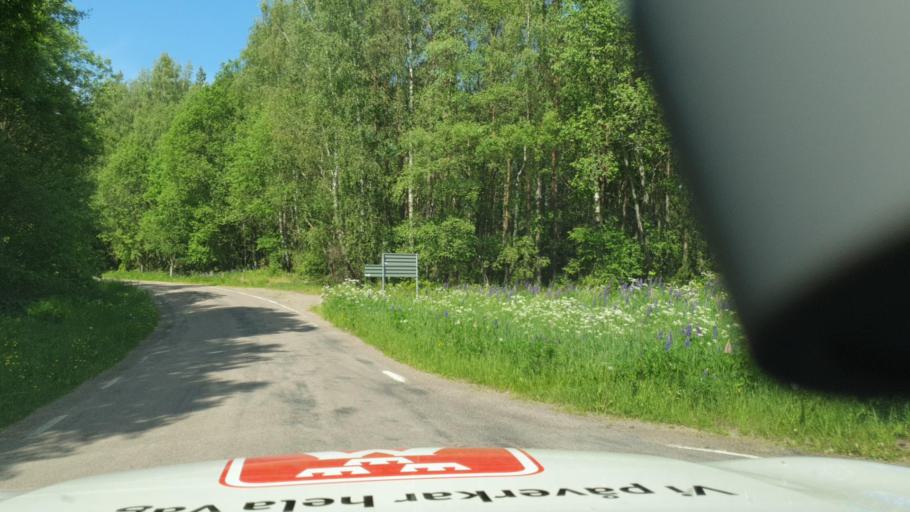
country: SE
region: Vaestra Goetaland
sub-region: Herrljunga Kommun
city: Herrljunga
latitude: 58.1190
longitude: 13.1085
